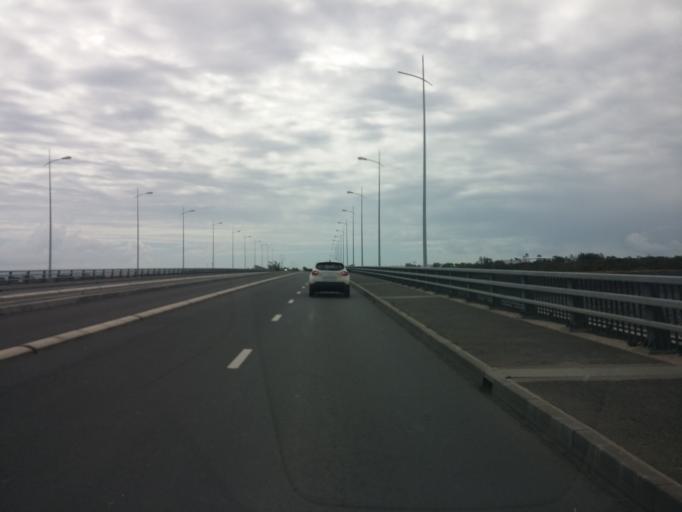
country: RE
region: Reunion
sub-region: Reunion
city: Le Port
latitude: -20.9586
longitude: 55.2940
